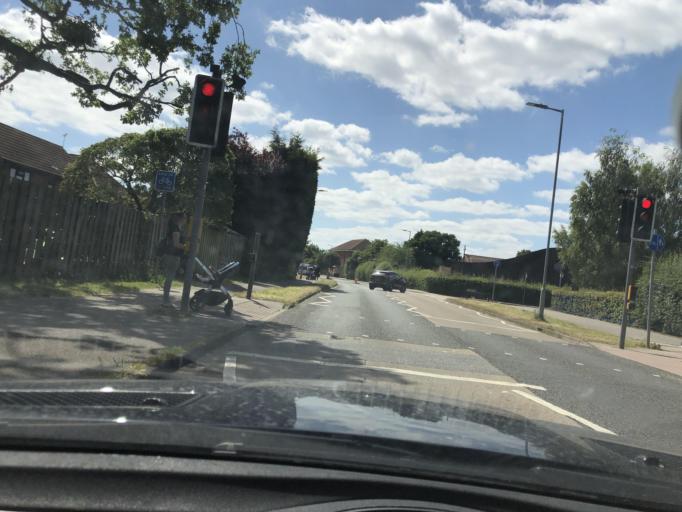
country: GB
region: England
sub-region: Essex
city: Chelmsford
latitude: 51.7513
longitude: 0.5001
